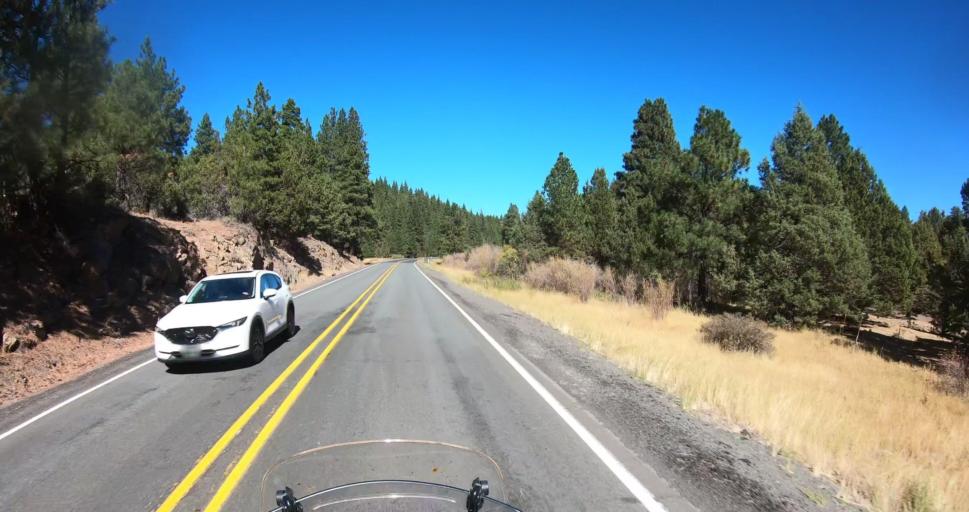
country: US
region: Oregon
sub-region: Lake County
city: Lakeview
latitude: 42.4010
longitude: -120.2929
